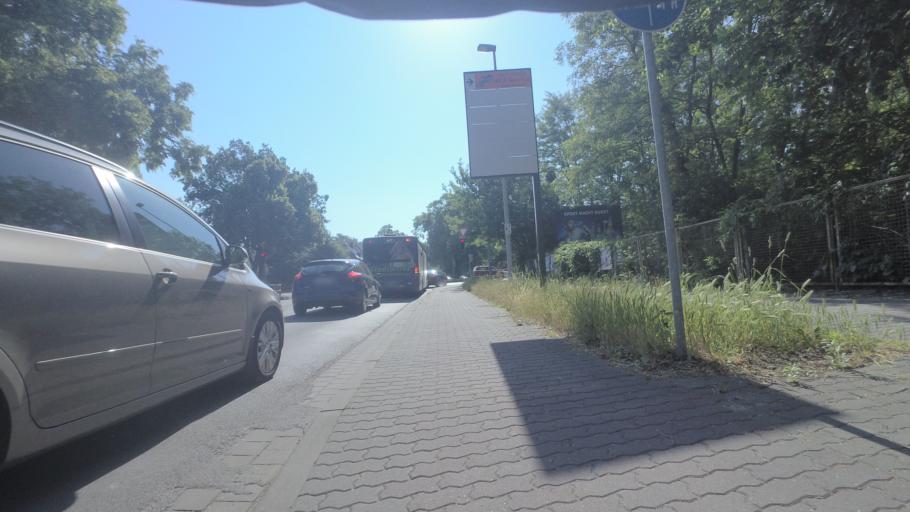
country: DE
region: Saxony-Anhalt
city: Dessau
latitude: 51.8364
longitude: 12.2152
